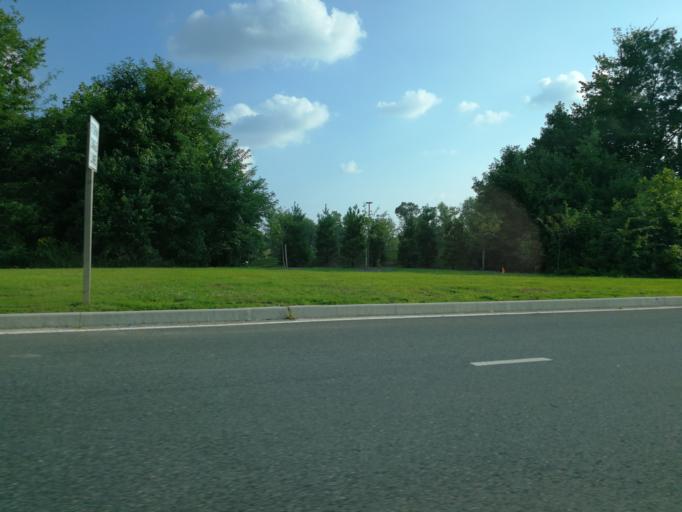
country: US
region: Maryland
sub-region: Harford County
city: Riverside
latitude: 39.4888
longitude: -76.2229
